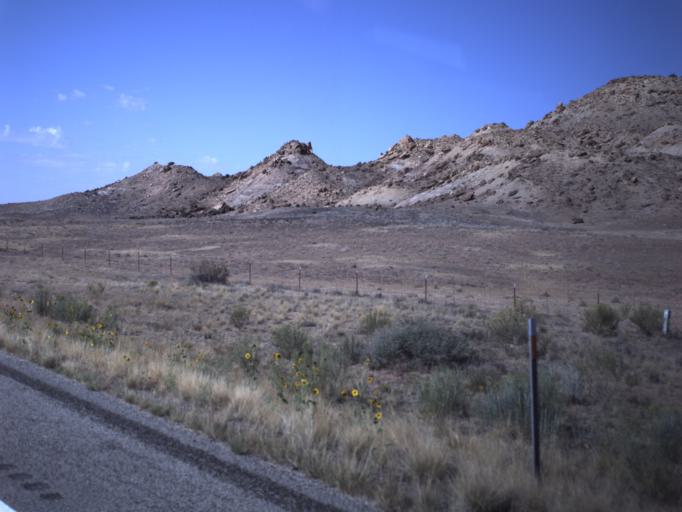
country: US
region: Utah
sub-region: San Juan County
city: Blanding
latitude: 37.4194
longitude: -109.4771
